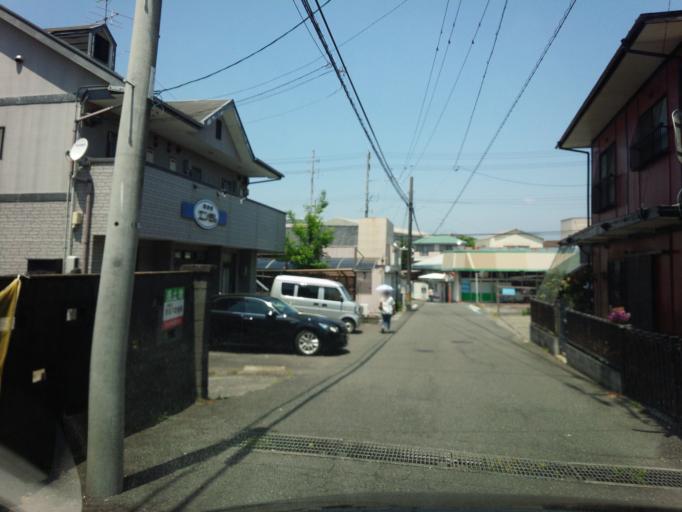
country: JP
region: Shizuoka
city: Shizuoka-shi
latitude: 34.9841
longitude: 138.5081
